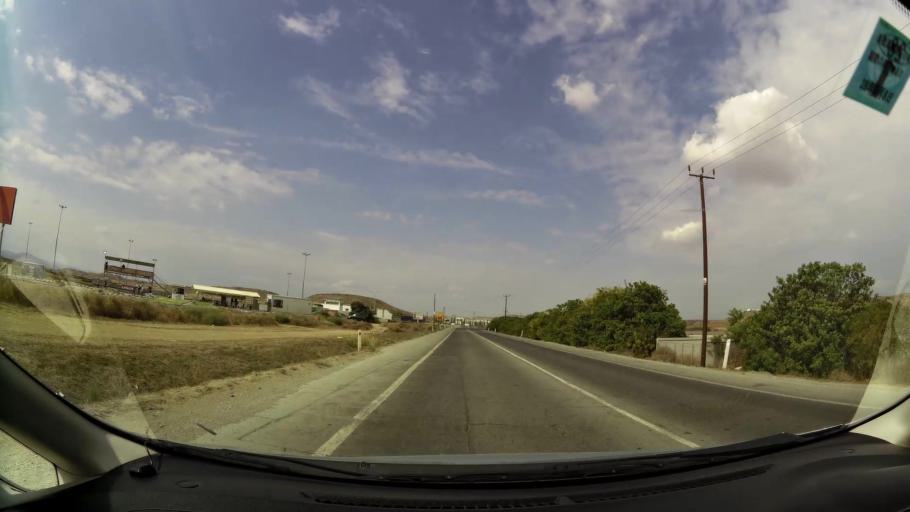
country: CY
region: Lefkosia
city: Dali
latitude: 35.0531
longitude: 33.3771
